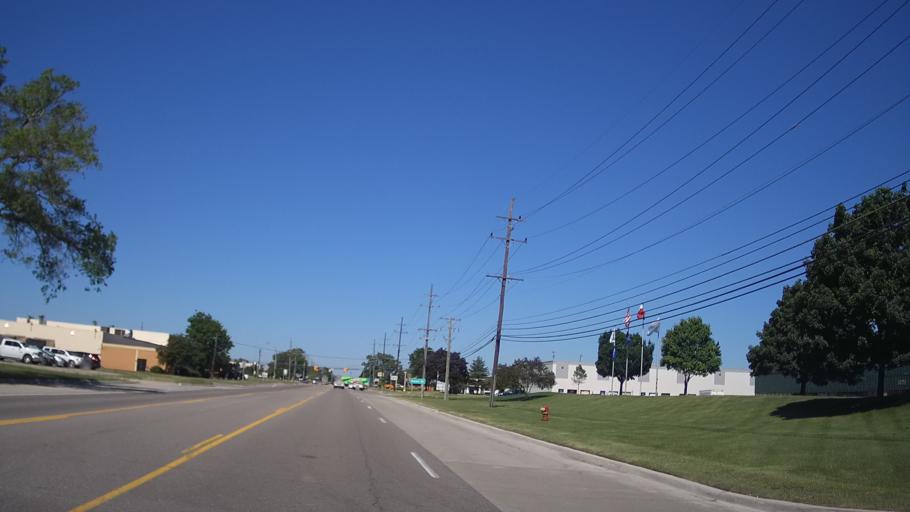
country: US
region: Michigan
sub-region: Macomb County
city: Sterling Heights
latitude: 42.5944
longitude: -83.0471
